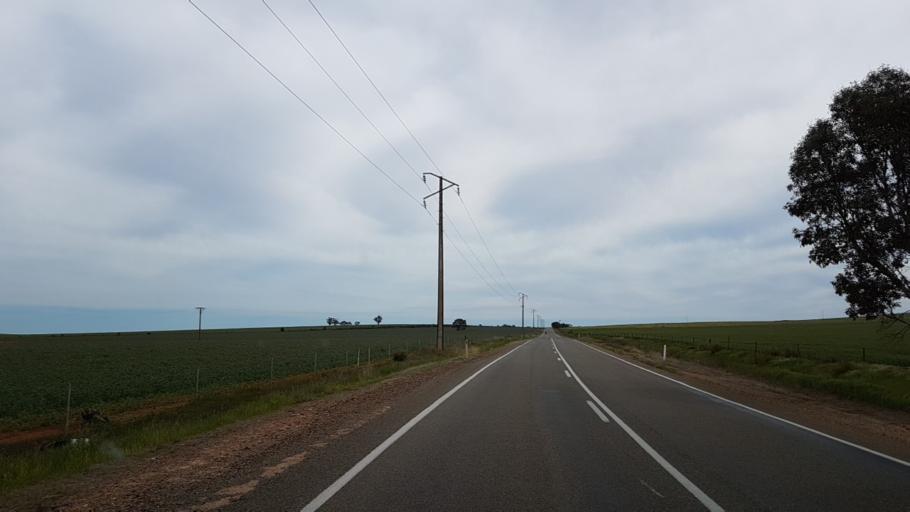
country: AU
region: South Australia
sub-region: Port Pirie City and Dists
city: Crystal Brook
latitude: -33.2746
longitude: 138.3113
